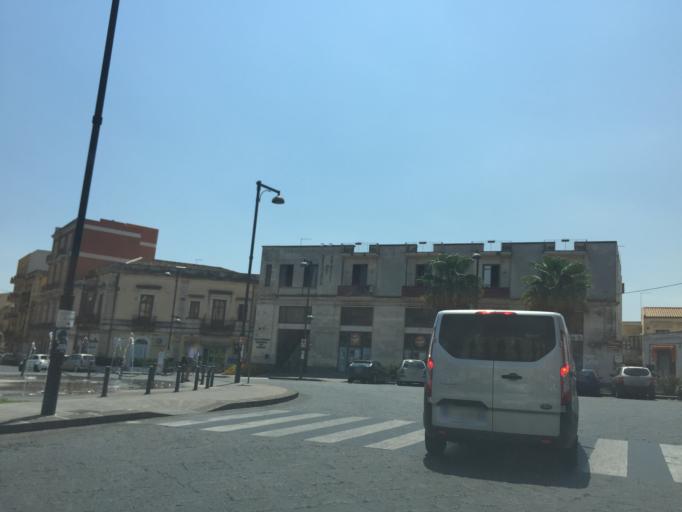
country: IT
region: Sicily
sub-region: Provincia di Siracusa
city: Siracusa
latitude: 37.0667
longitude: 15.2838
